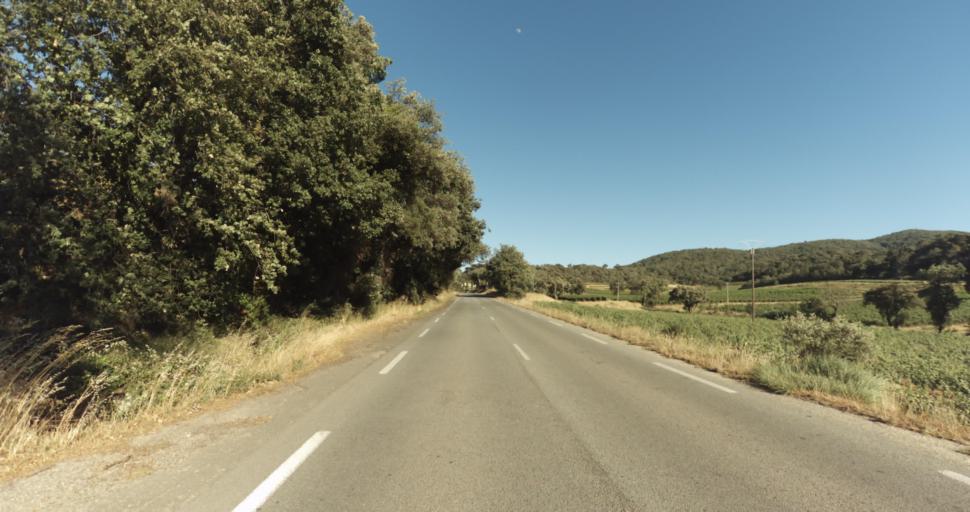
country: FR
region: Provence-Alpes-Cote d'Azur
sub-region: Departement du Var
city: Gassin
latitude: 43.2404
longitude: 6.5993
